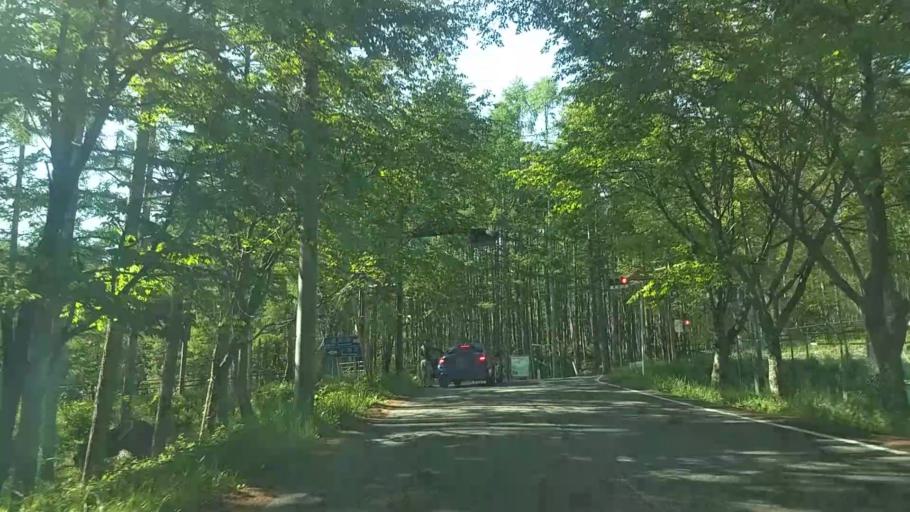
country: JP
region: Nagano
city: Chino
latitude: 35.8997
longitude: 138.3509
